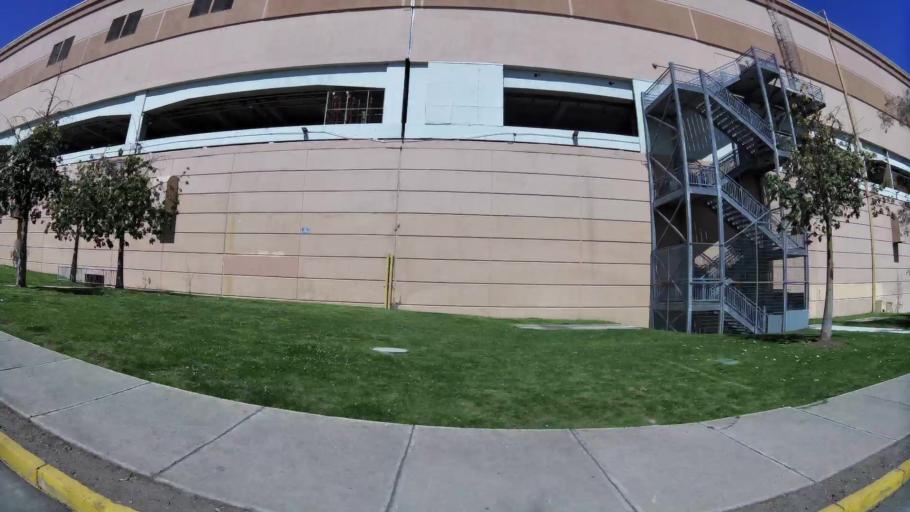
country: CL
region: Santiago Metropolitan
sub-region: Provincia de Santiago
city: Villa Presidente Frei, Nunoa, Santiago, Chile
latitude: -33.4275
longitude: -70.5413
